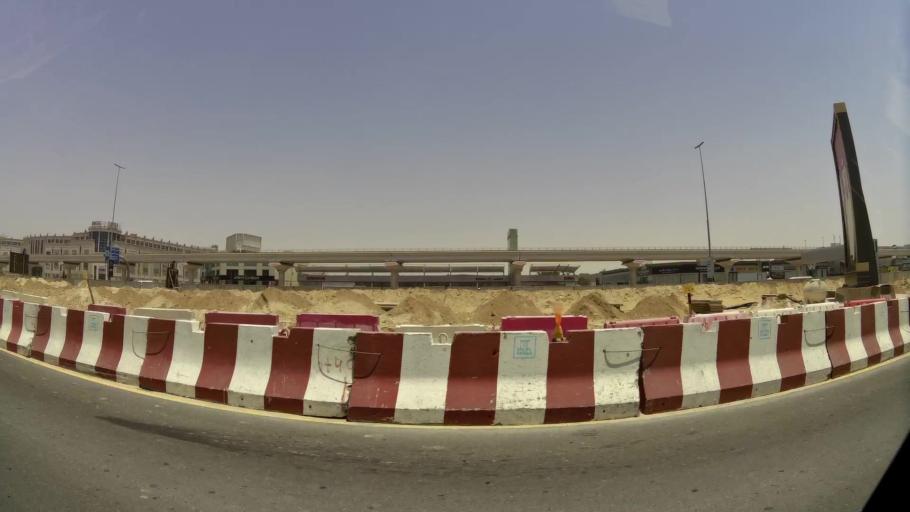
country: AE
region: Dubai
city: Dubai
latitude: 25.1691
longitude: 55.2382
